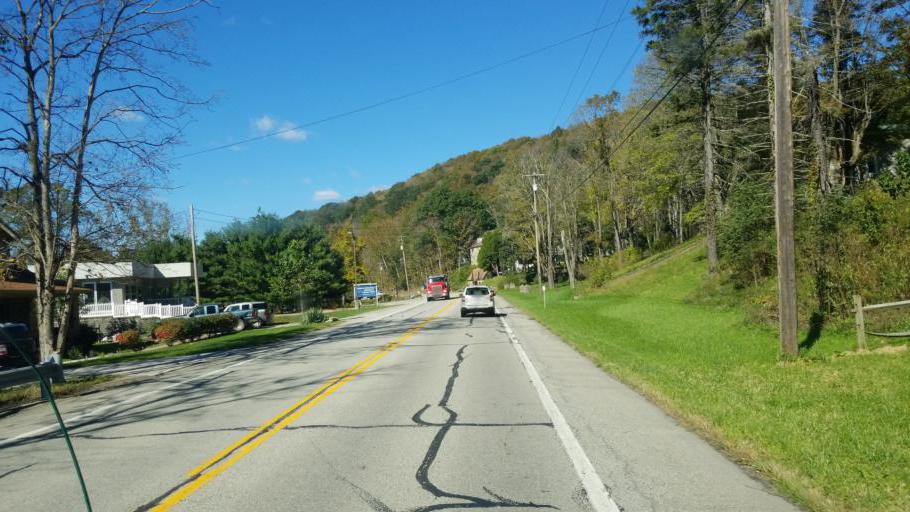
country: US
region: Pennsylvania
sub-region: Westmoreland County
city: Ligonier
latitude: 40.2287
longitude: -79.2208
